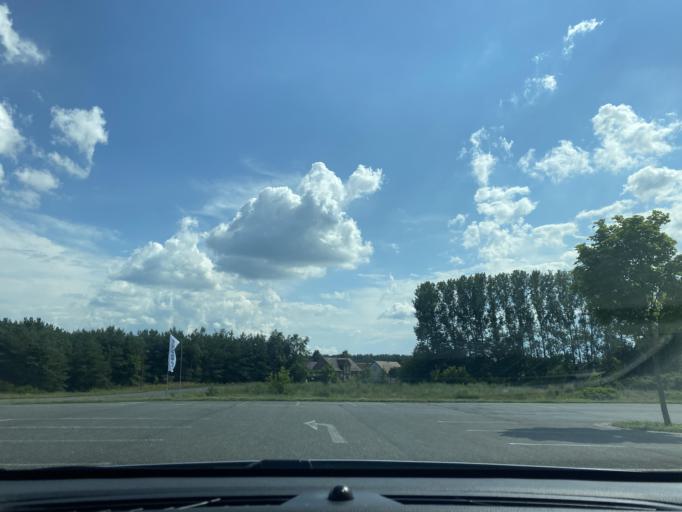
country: DE
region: Saxony
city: Boxberg
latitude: 51.4353
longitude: 14.6037
